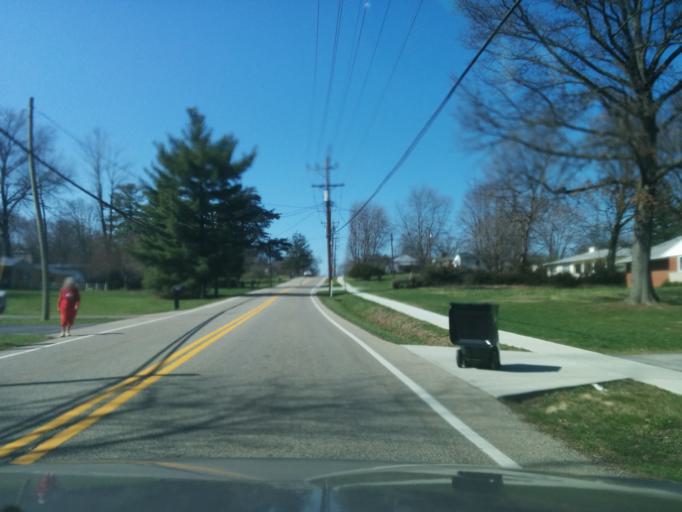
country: US
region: Ohio
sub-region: Hamilton County
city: Northgate
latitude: 39.2356
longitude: -84.6041
